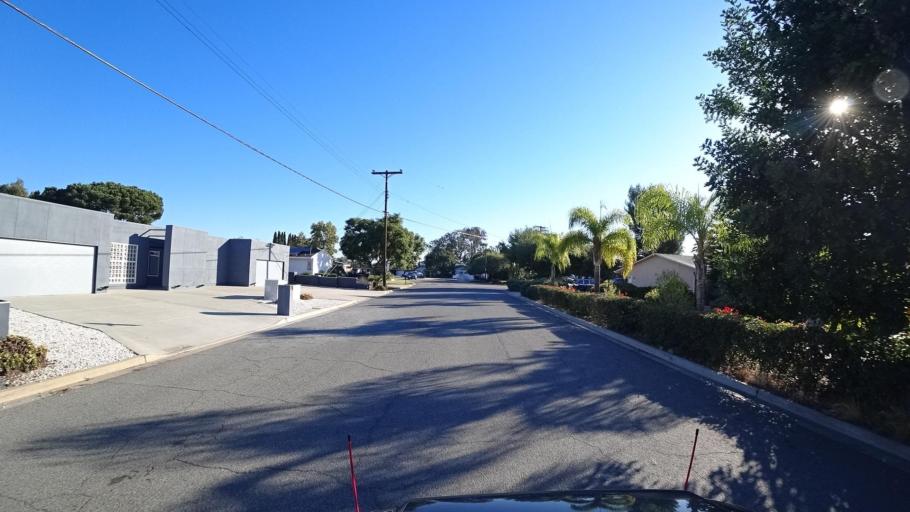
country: US
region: California
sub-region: San Diego County
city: Bonita
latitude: 32.6709
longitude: -117.0270
